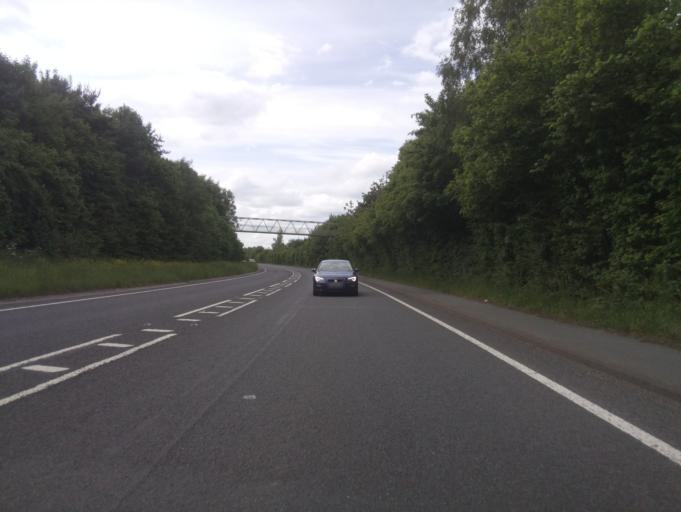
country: GB
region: England
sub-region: Worcestershire
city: Worcester
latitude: 52.1788
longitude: -2.2510
